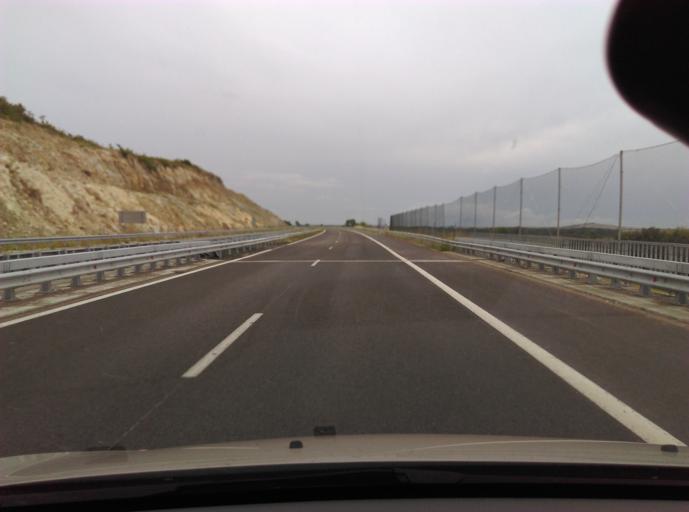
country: BG
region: Stara Zagora
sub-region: Obshtina Chirpan
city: Chirpan
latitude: 42.1031
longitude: 25.4217
